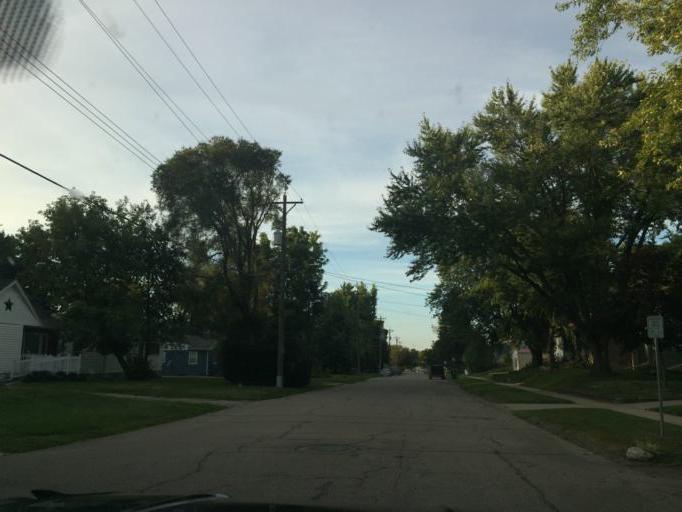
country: US
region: Minnesota
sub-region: Olmsted County
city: Rochester
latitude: 44.0185
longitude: -92.4921
